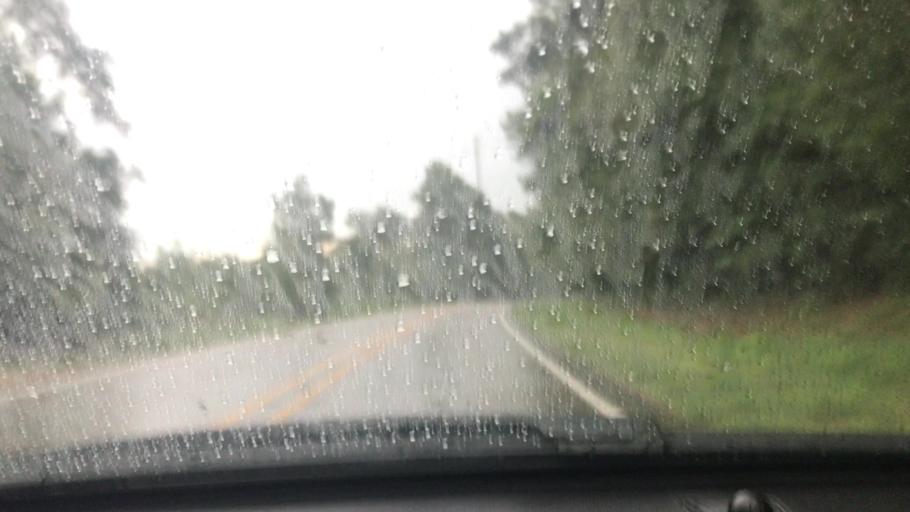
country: US
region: Mississippi
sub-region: Pike County
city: Summit
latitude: 31.3164
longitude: -90.5265
